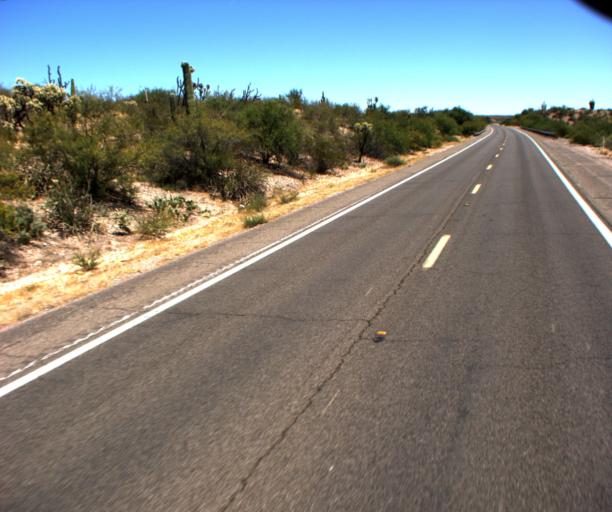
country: US
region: Arizona
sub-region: Pinal County
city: Mammoth
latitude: 32.8203
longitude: -110.6935
